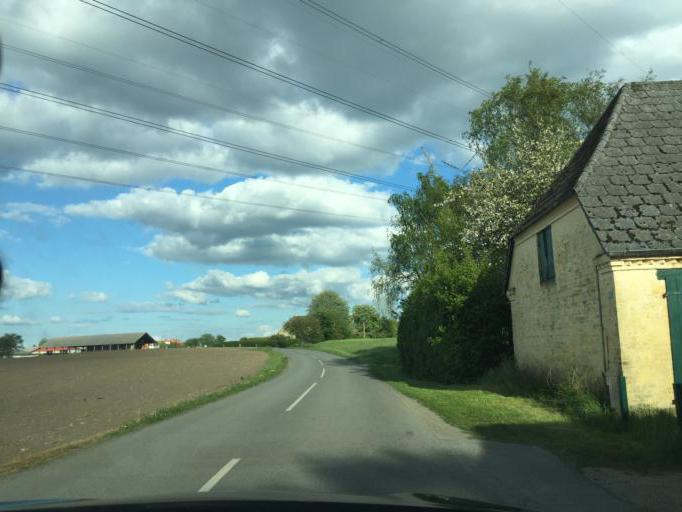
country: DK
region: South Denmark
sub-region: Odense Kommune
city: Bellinge
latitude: 55.3677
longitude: 10.2920
